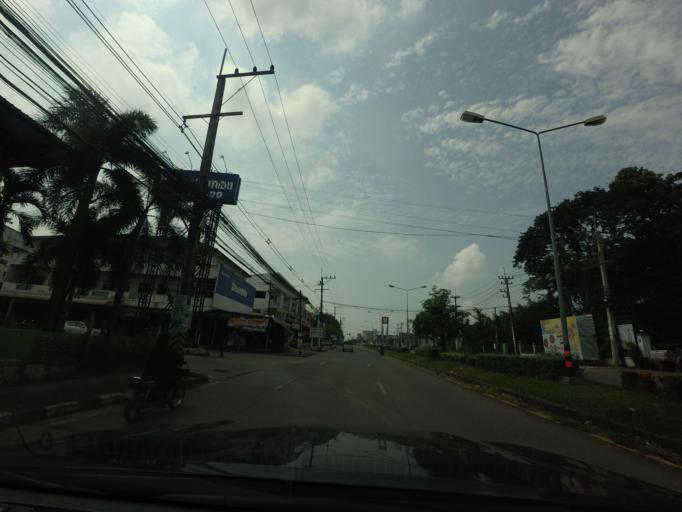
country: TH
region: Phrae
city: Phrae
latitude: 18.1271
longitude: 100.1430
